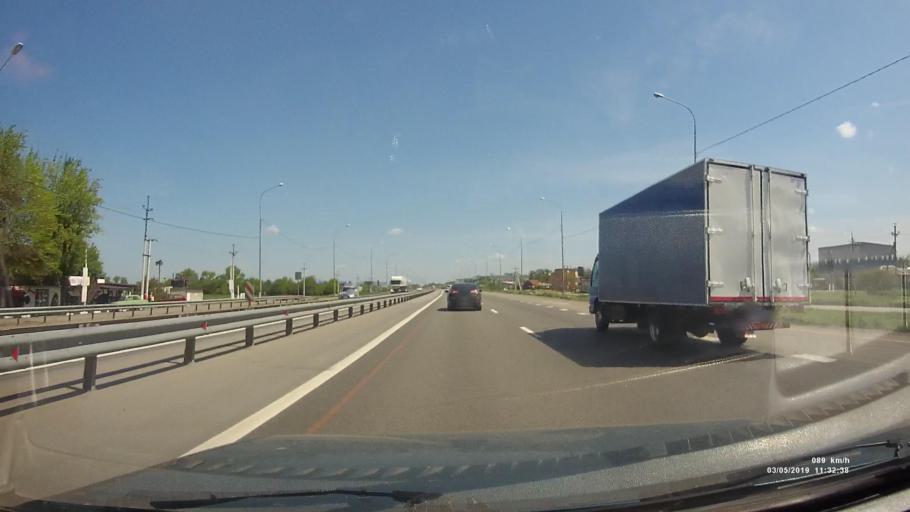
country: RU
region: Rostov
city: Bataysk
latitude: 47.1176
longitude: 39.8563
